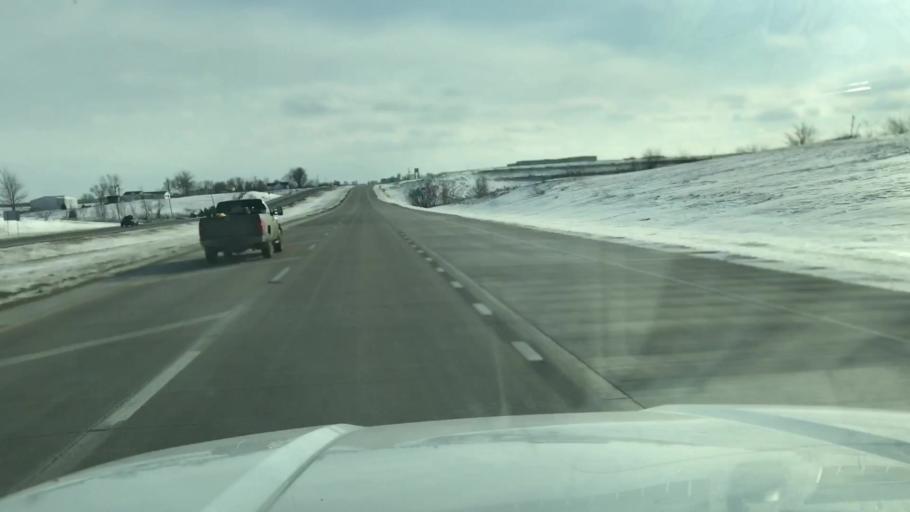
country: US
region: Missouri
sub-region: Nodaway County
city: Maryville
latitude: 40.3067
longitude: -94.8748
